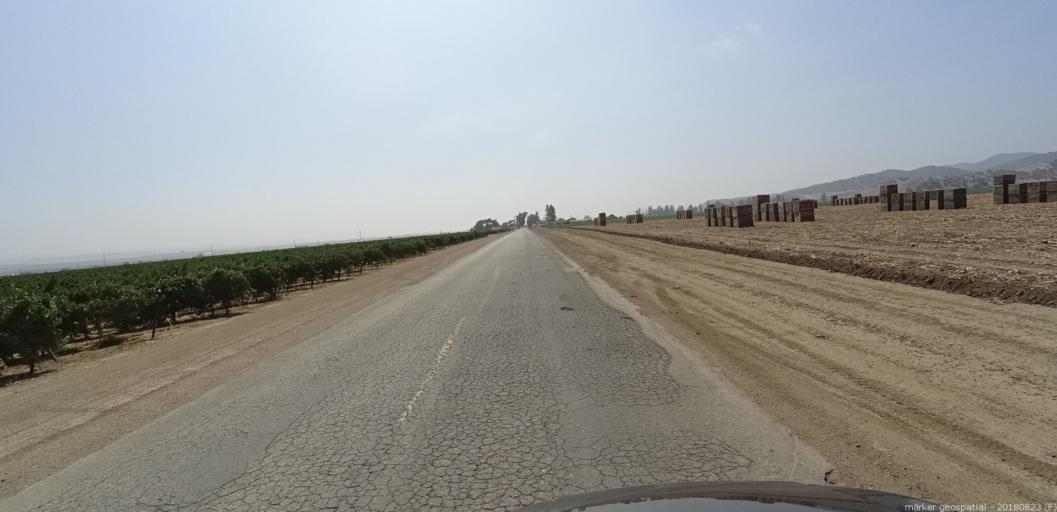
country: US
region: California
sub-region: Monterey County
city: King City
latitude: 36.2371
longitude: -121.1808
